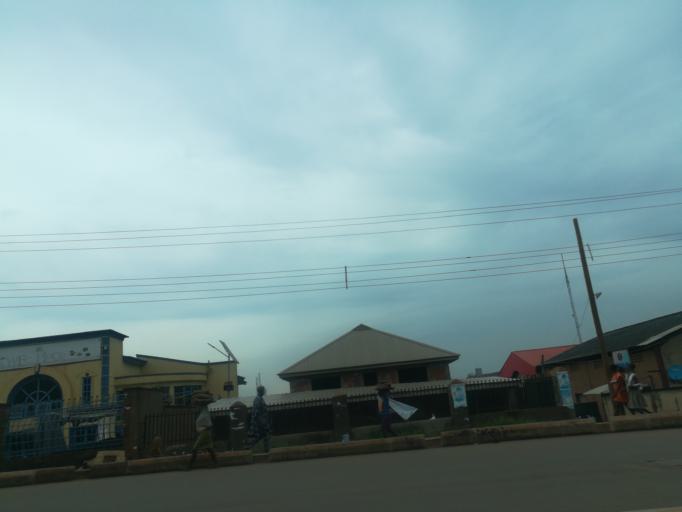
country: NG
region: Oyo
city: Ibadan
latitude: 7.3952
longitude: 3.9235
